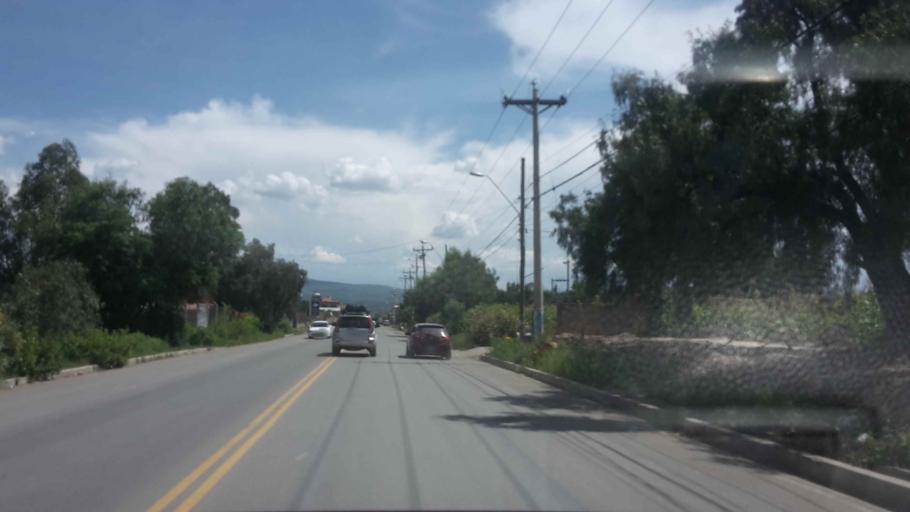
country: BO
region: Cochabamba
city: Cochabamba
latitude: -17.3620
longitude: -66.2293
